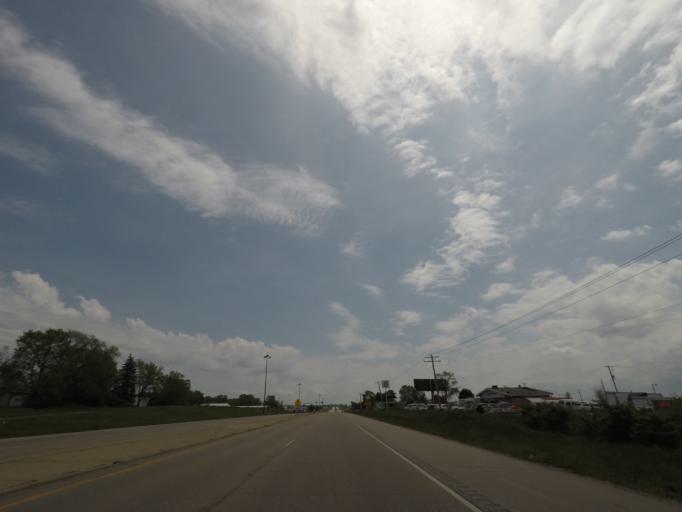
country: US
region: Illinois
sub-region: McLean County
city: Bloomington
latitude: 40.4324
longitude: -88.9906
